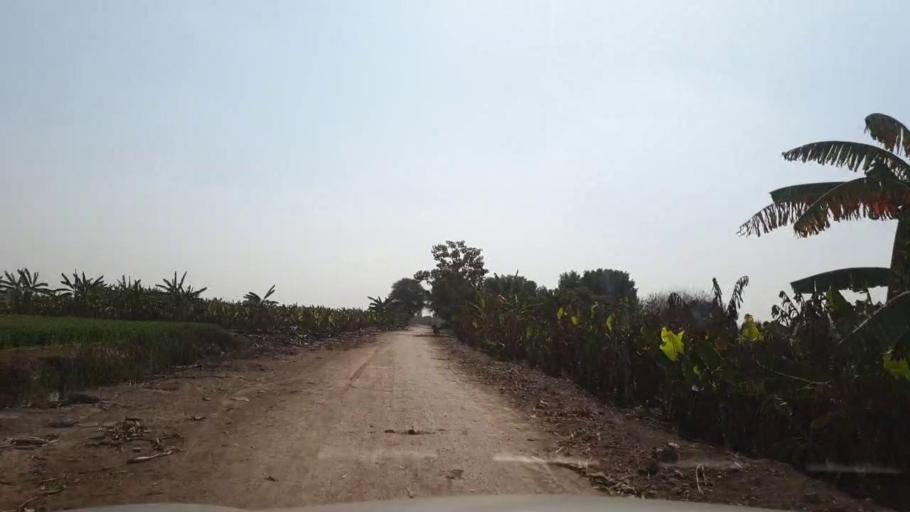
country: PK
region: Sindh
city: Tando Allahyar
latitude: 25.5493
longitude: 68.6982
